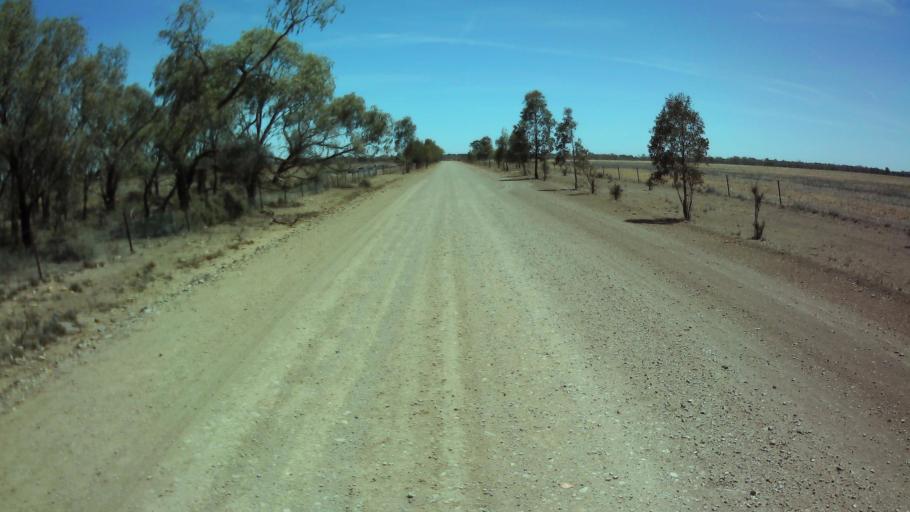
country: AU
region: New South Wales
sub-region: Bland
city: West Wyalong
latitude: -33.8196
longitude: 147.6460
